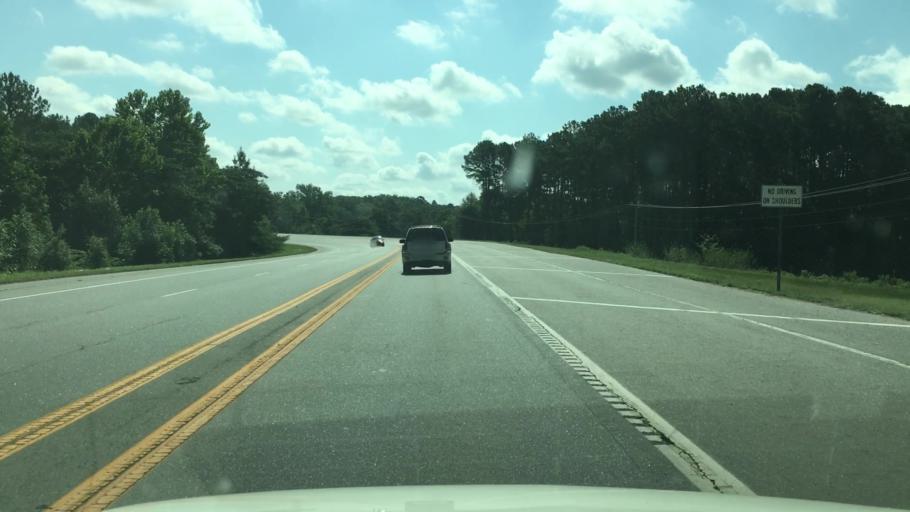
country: US
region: Arkansas
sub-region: Garland County
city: Piney
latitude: 34.5072
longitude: -93.1869
